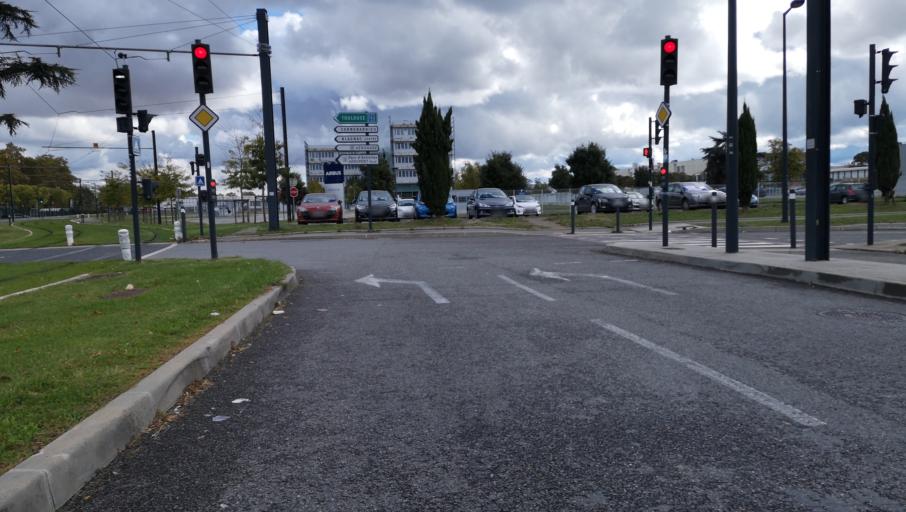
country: FR
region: Midi-Pyrenees
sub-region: Departement de la Haute-Garonne
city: Blagnac
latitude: 43.6252
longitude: 1.3824
